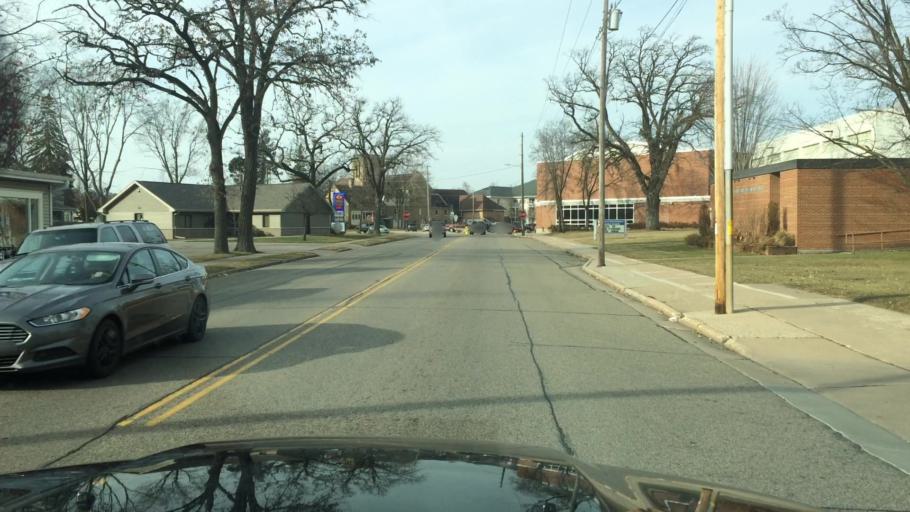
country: US
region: Wisconsin
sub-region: Waupaca County
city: Waupaca
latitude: 44.3552
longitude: -89.0799
